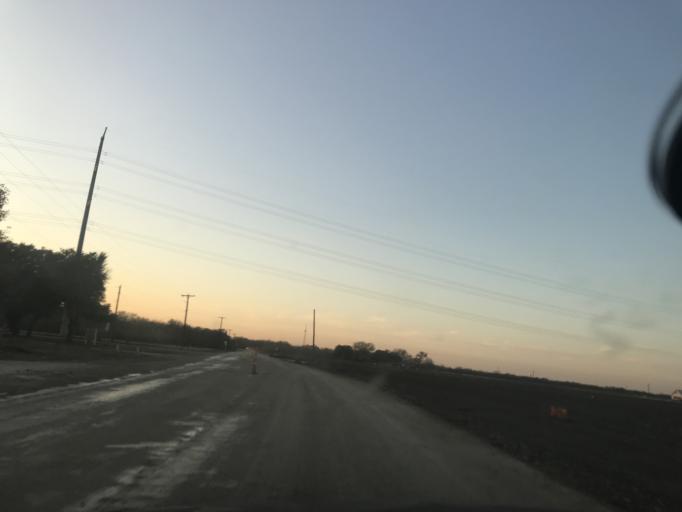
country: US
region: Texas
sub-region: Williamson County
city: Hutto
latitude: 30.5103
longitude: -97.5231
